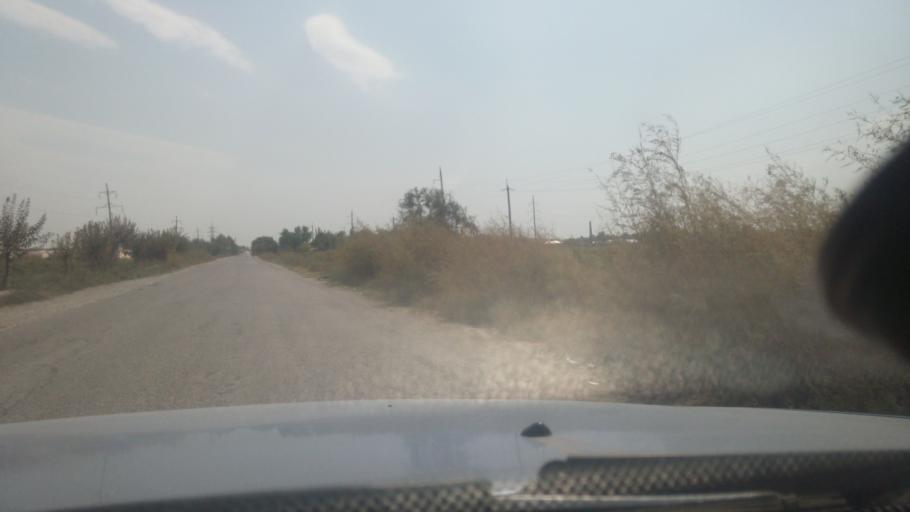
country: UZ
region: Sirdaryo
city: Guliston
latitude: 40.5321
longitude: 68.7663
